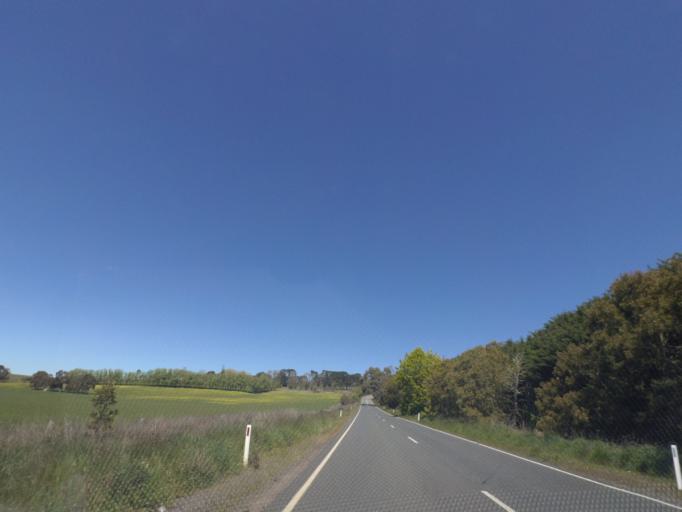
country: AU
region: Victoria
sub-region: Hume
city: Sunbury
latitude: -37.2994
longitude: 144.6888
